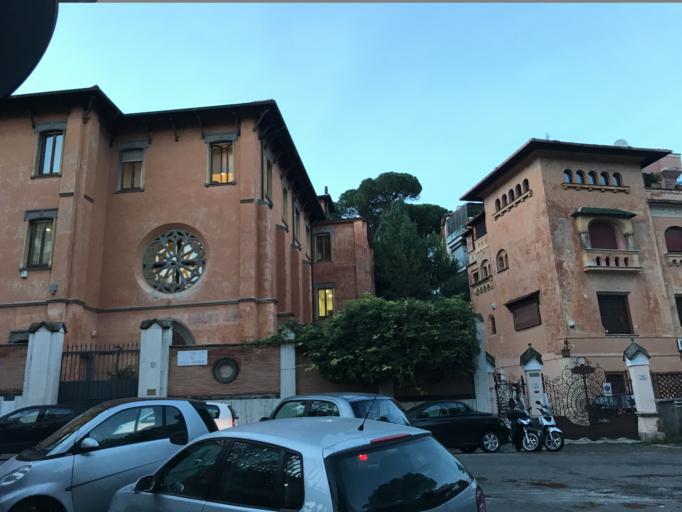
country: IT
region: Latium
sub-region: Citta metropolitana di Roma Capitale
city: Rome
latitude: 41.9097
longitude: 12.5073
